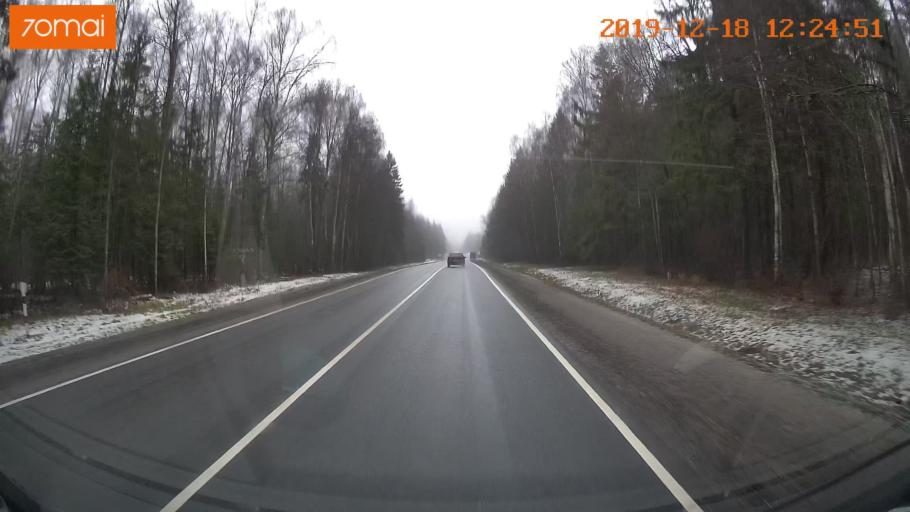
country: RU
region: Moskovskaya
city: Novopetrovskoye
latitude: 56.0301
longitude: 36.5005
